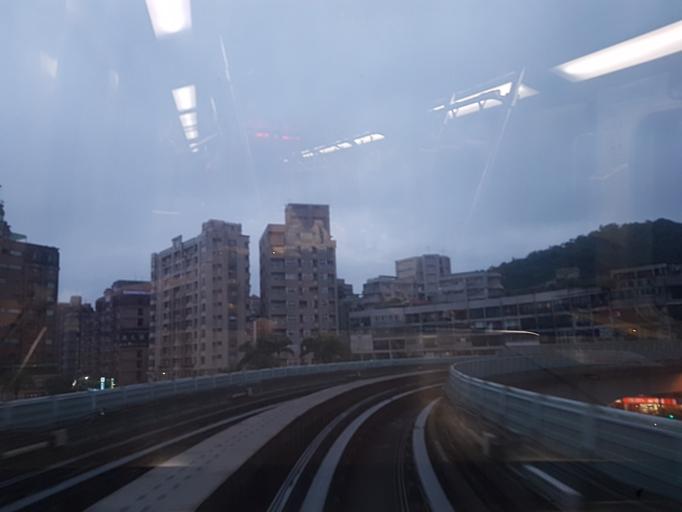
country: TW
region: Taipei
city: Taipei
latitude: 25.0730
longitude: 121.6064
